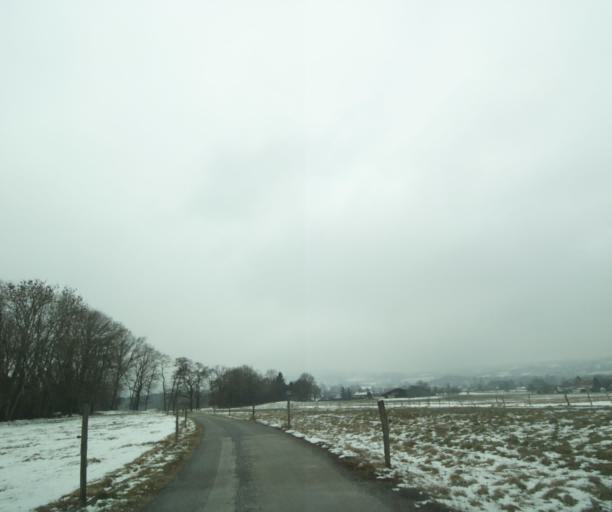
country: FR
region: Rhone-Alpes
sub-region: Departement de la Haute-Savoie
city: Reignier-Esery
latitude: 46.1345
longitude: 6.2895
